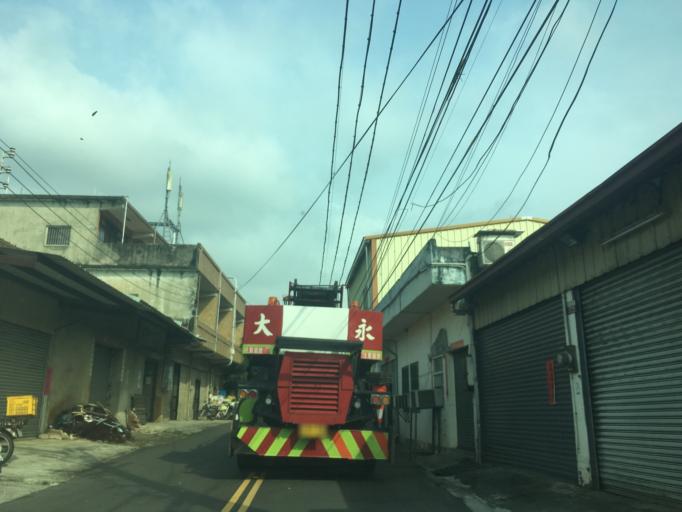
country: TW
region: Taiwan
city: Fengyuan
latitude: 24.2328
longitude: 120.7480
